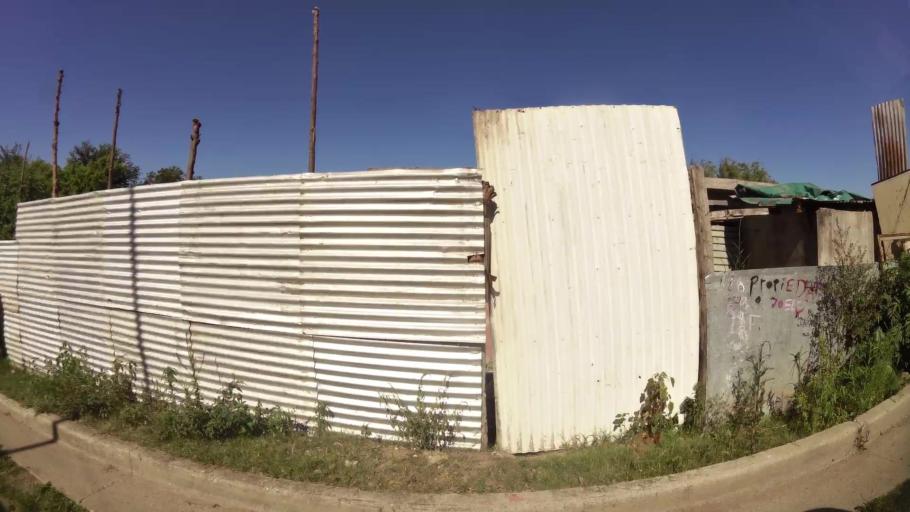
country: AR
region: Cordoba
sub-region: Departamento de Capital
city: Cordoba
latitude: -31.4039
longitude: -64.1505
